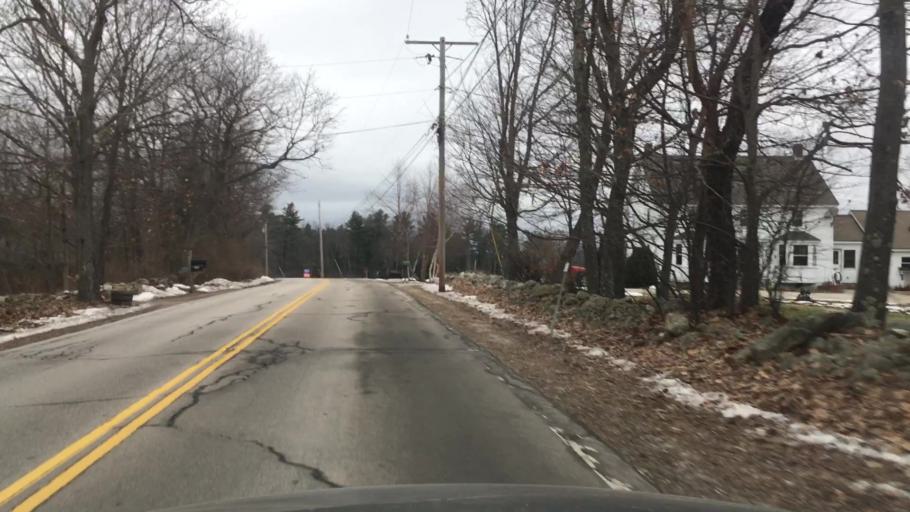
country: US
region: New Hampshire
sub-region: Hillsborough County
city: Mont Vernon
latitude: 42.9399
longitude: -71.6140
